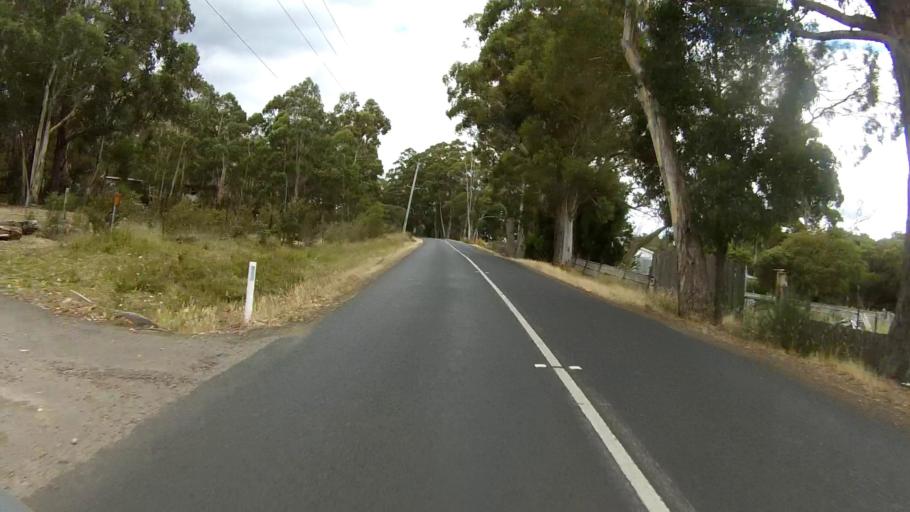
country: AU
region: Tasmania
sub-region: Kingborough
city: Margate
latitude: -42.9638
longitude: 147.2100
